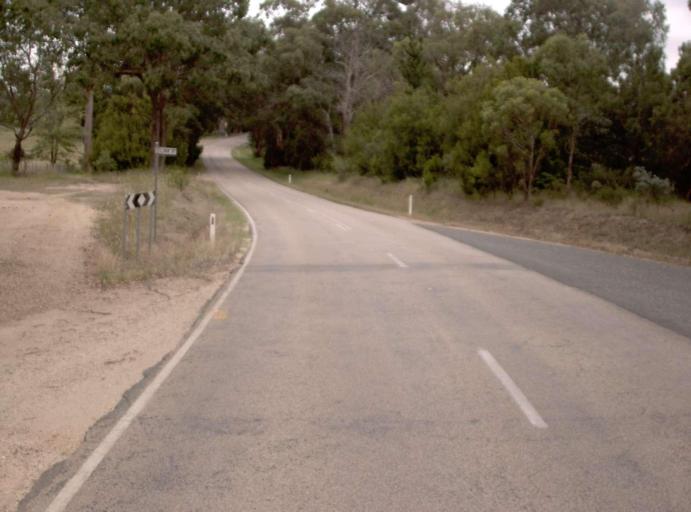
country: AU
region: Victoria
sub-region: East Gippsland
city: Bairnsdale
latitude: -37.7888
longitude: 147.6054
